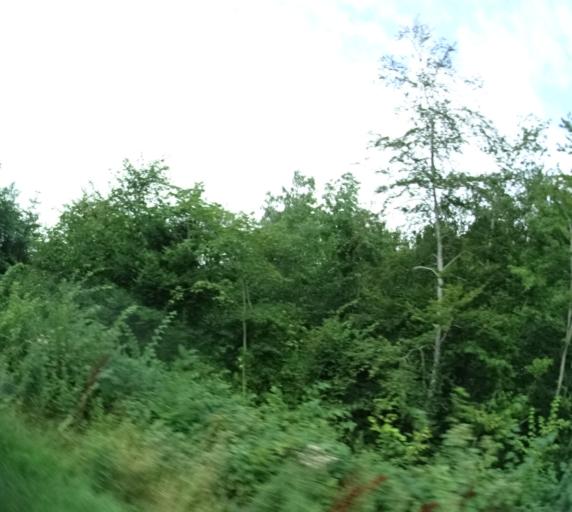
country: DK
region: Central Jutland
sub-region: Syddjurs Kommune
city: Ryomgard
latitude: 56.3974
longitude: 10.5168
